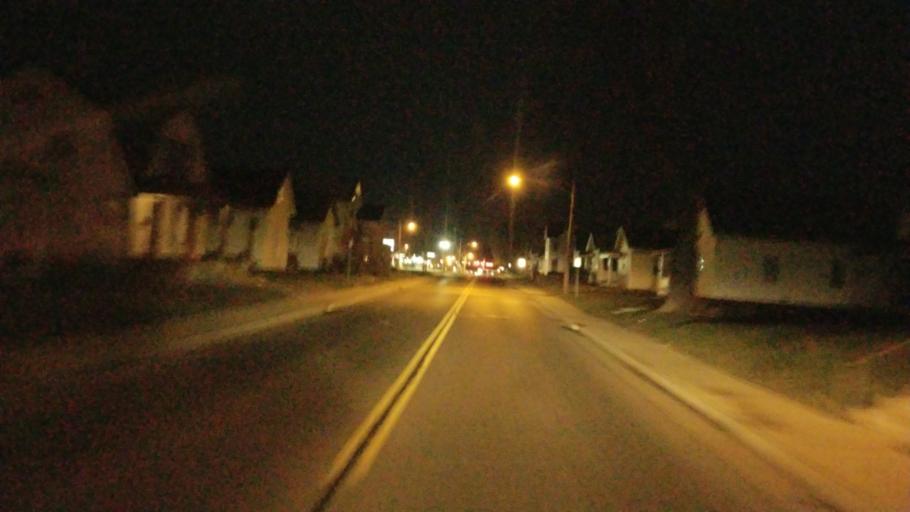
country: US
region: Ohio
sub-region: Fayette County
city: Washington Court House
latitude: 39.5310
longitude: -83.4474
